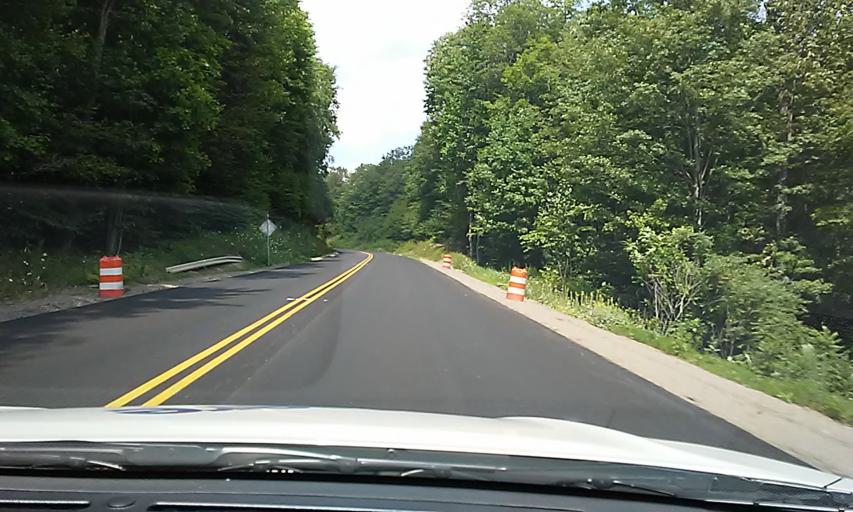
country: US
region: Pennsylvania
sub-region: Cameron County
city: Emporium
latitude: 41.6553
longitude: -78.1918
